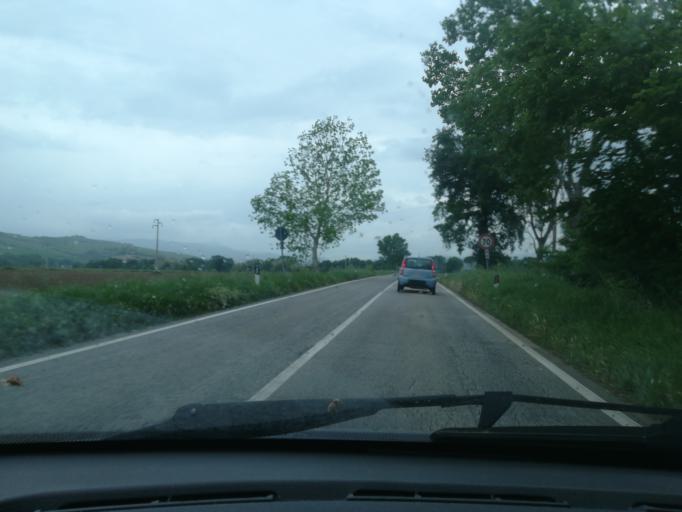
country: IT
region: The Marches
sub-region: Provincia di Macerata
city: Treia
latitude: 43.2715
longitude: 13.2792
